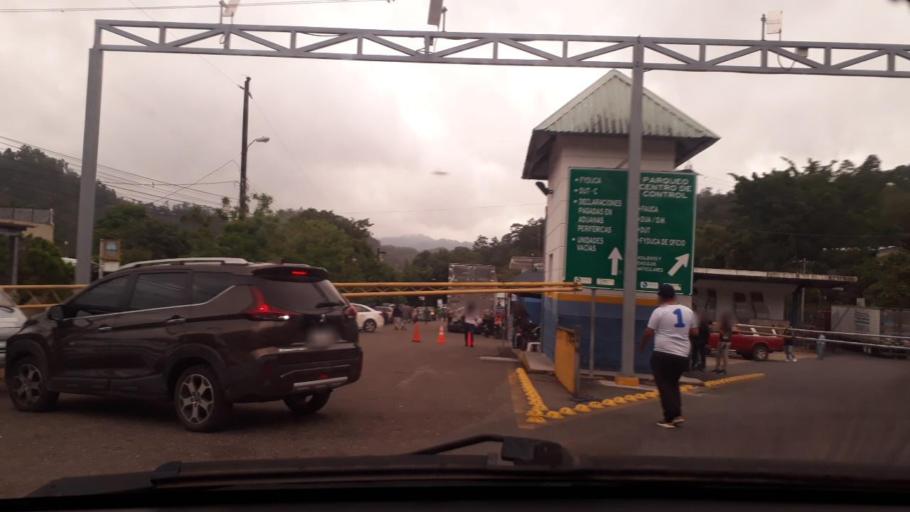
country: GT
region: Chiquimula
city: Esquipulas
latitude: 14.5345
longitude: -89.2794
